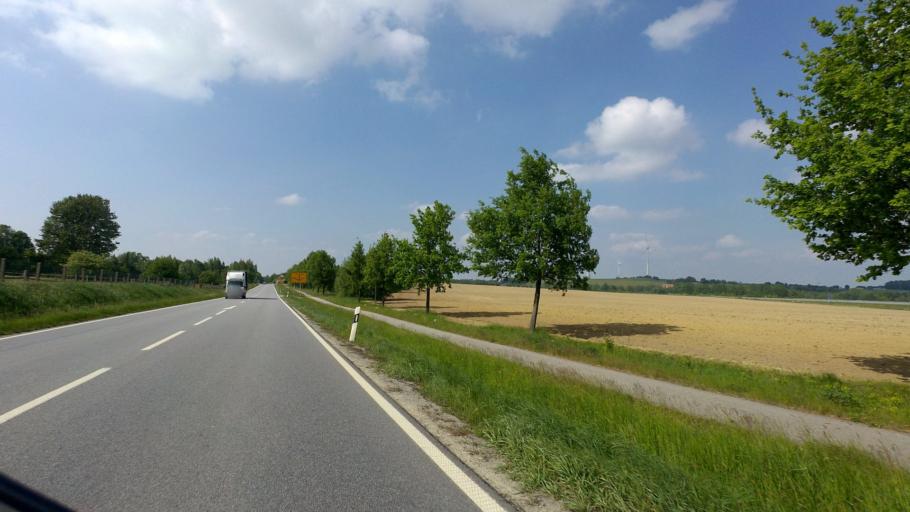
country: DE
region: Saxony
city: Lobau
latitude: 51.1144
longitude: 14.6458
